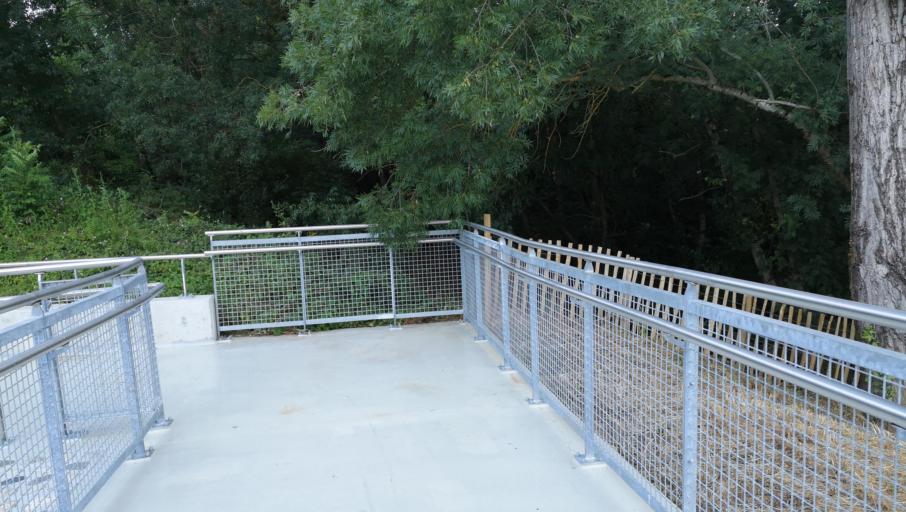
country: FR
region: Midi-Pyrenees
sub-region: Departement de la Haute-Garonne
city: Colomiers
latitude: 43.5961
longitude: 1.3714
